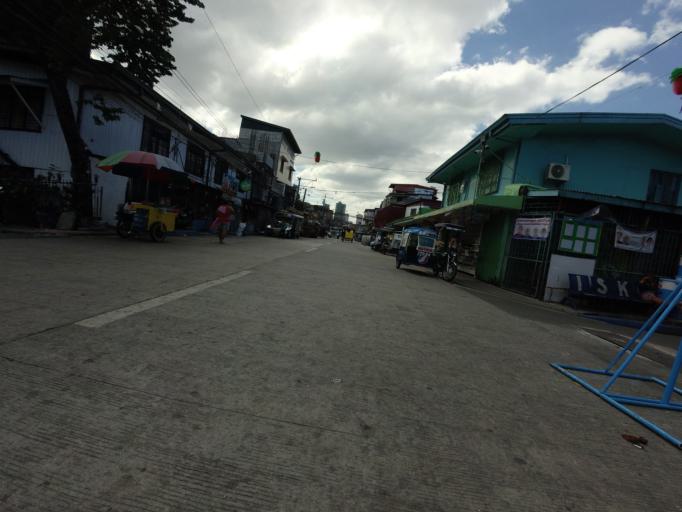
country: PH
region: Metro Manila
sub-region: City of Manila
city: Quiapo
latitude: 14.5743
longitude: 121.0066
